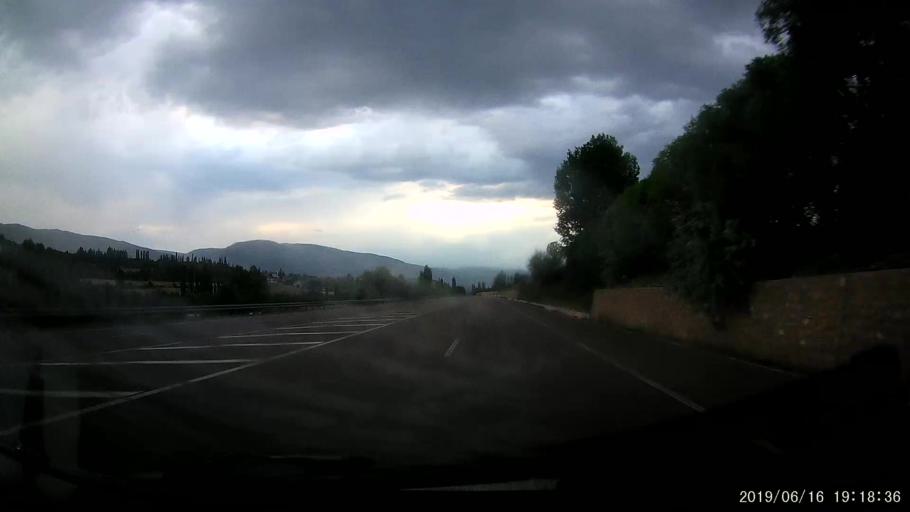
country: TR
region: Sivas
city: Akincilar
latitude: 40.0953
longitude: 38.4530
